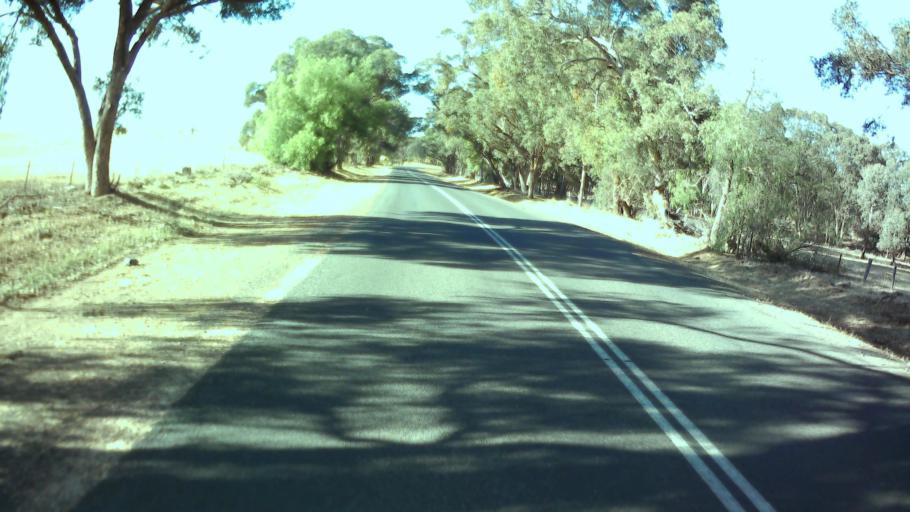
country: AU
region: New South Wales
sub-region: Weddin
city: Grenfell
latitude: -33.9957
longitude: 148.1324
